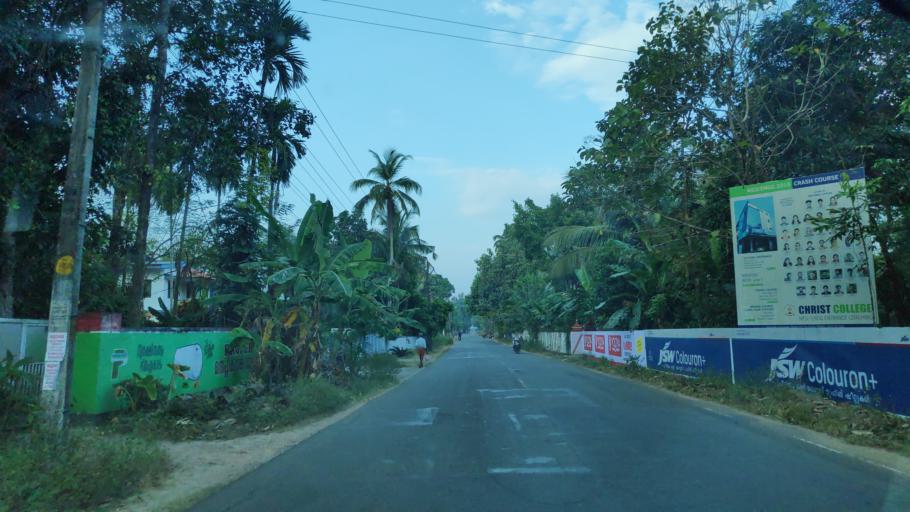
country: IN
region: Kerala
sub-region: Alappuzha
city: Shertallai
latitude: 9.6292
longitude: 76.3695
